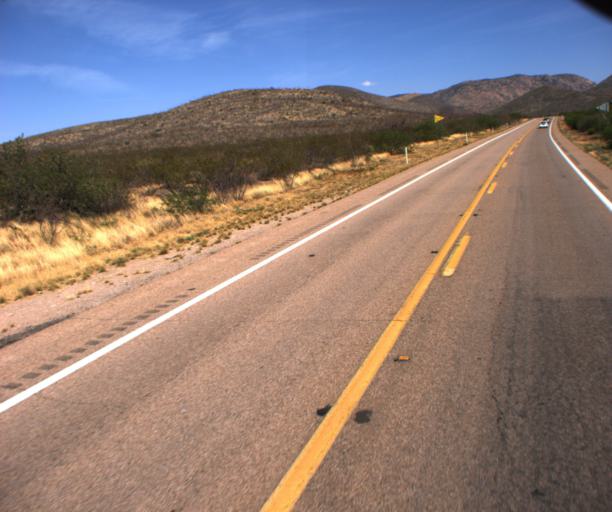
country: US
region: Arizona
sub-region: Cochise County
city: Bisbee
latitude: 31.5246
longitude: -110.0450
